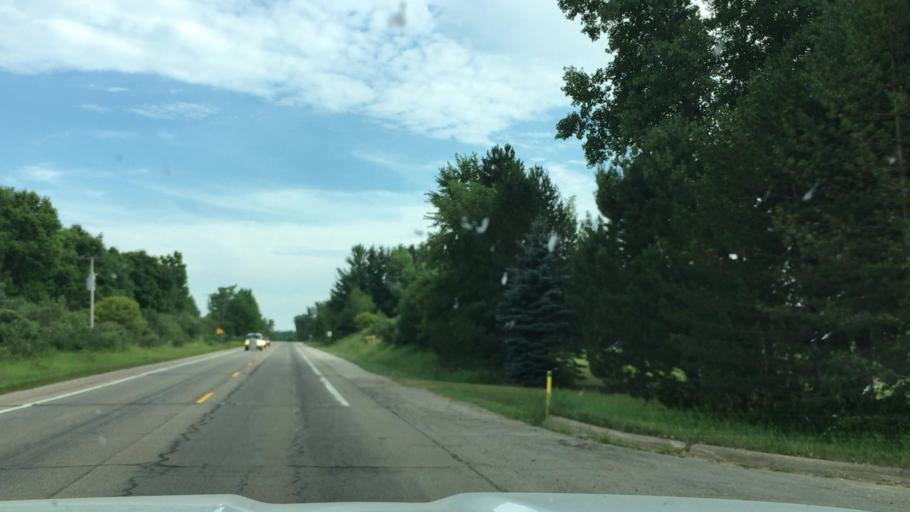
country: US
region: Michigan
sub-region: Sanilac County
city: Brown City
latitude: 43.1508
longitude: -83.0750
